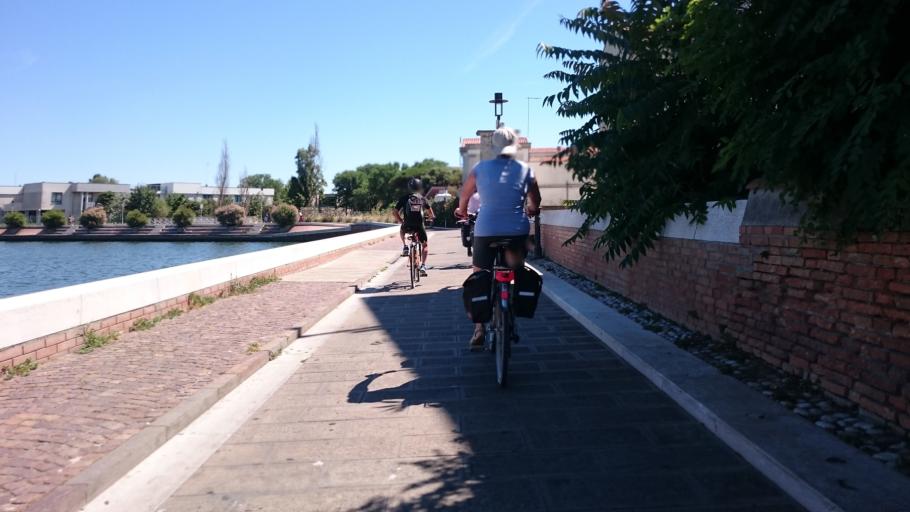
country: IT
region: Veneto
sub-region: Provincia di Venezia
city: Chioggia
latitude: 45.2043
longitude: 12.2783
